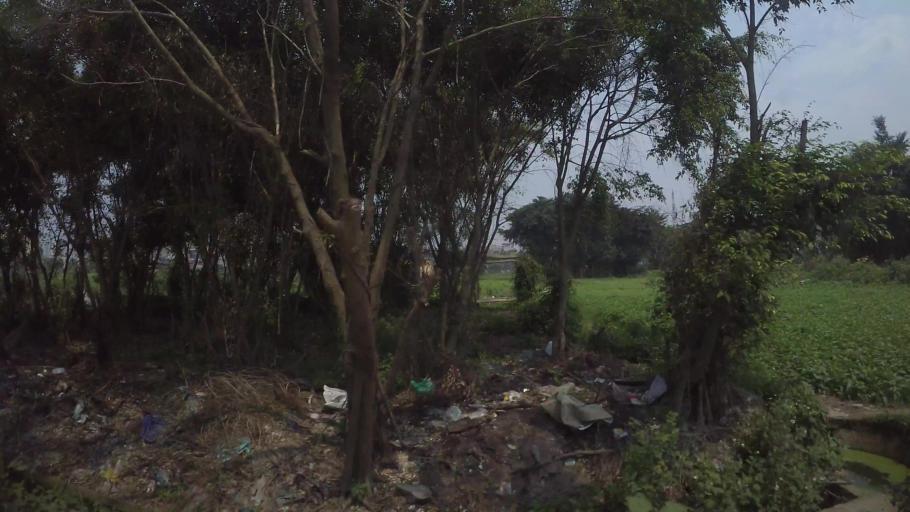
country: VN
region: Ha Noi
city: Van Dien
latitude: 20.9472
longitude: 105.8420
